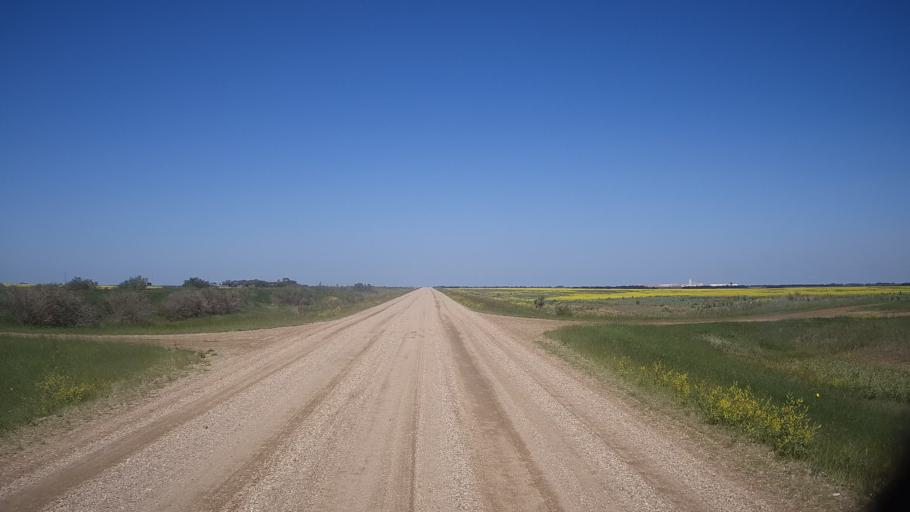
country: CA
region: Saskatchewan
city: Watrous
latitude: 51.8631
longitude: -105.9709
